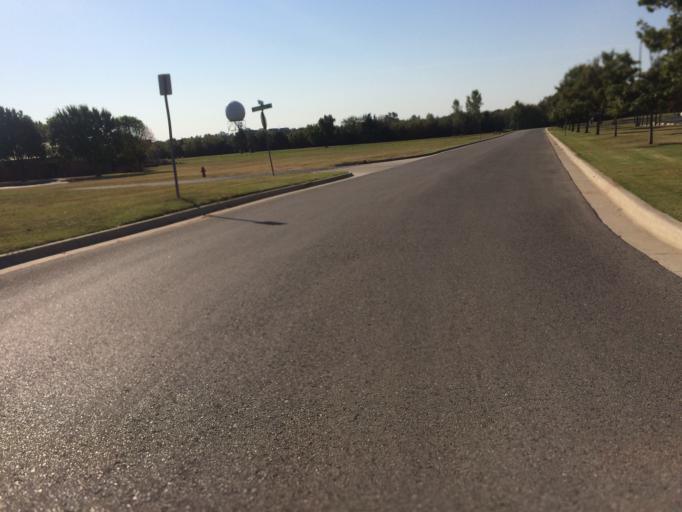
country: US
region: Oklahoma
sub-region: Cleveland County
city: Norman
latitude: 35.1833
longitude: -97.4354
